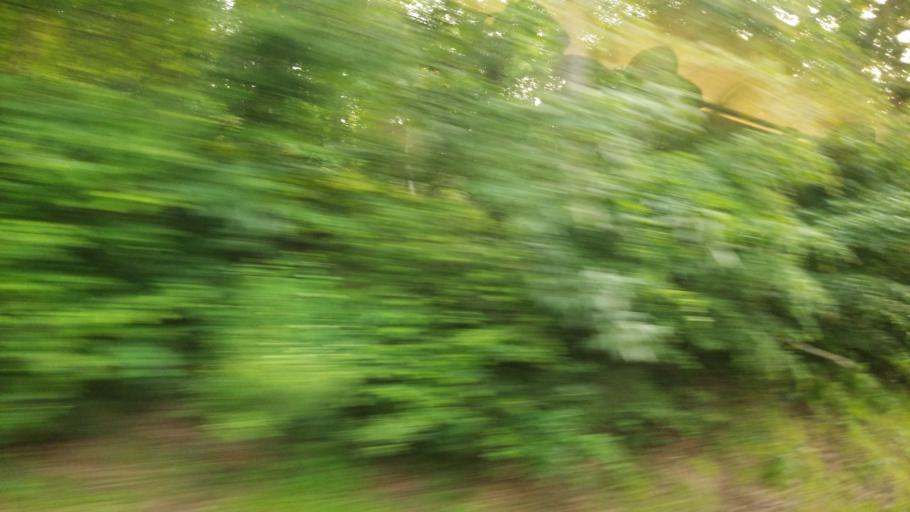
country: US
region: Virginia
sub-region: Prince William County
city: Yorkshire
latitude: 38.7781
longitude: -77.4257
